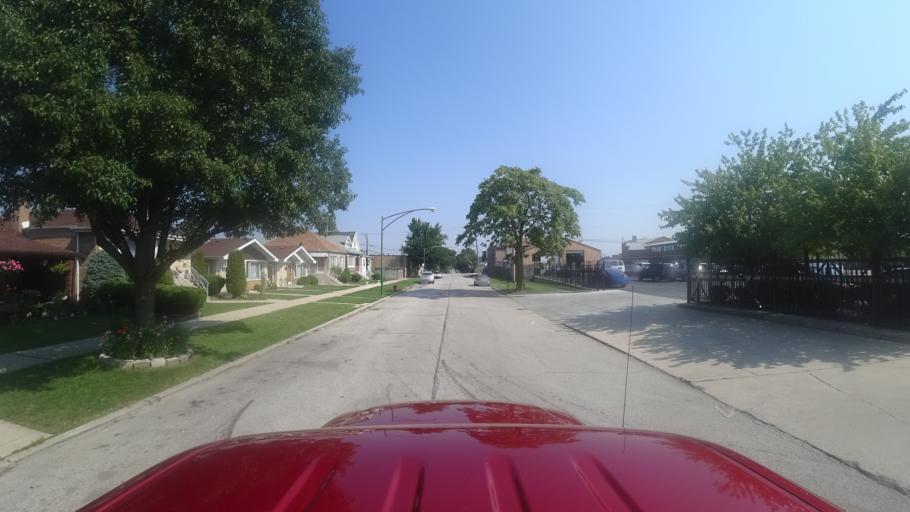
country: US
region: Illinois
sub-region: Cook County
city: Stickney
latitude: 41.7980
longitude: -87.7392
